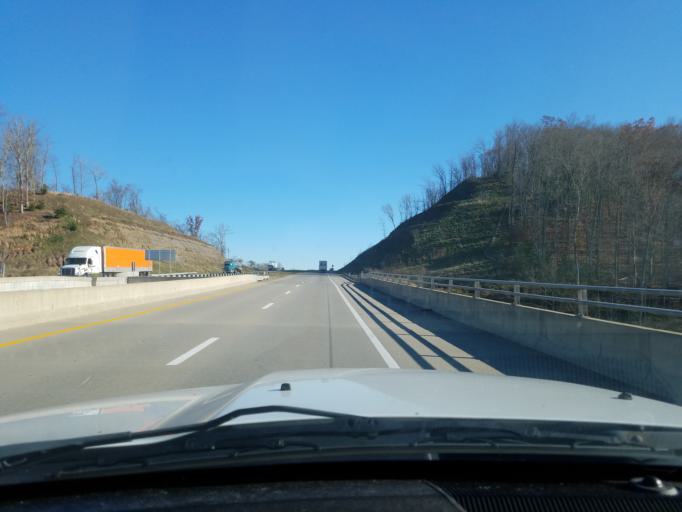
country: US
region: West Virginia
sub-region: Putnam County
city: Buffalo
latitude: 38.5555
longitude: -82.0005
